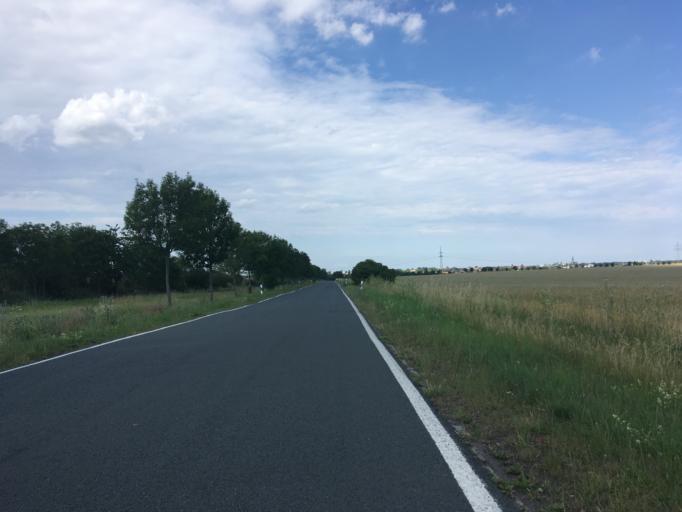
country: DE
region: Saxony-Anhalt
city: Baalberge
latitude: 51.7787
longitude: 11.7877
